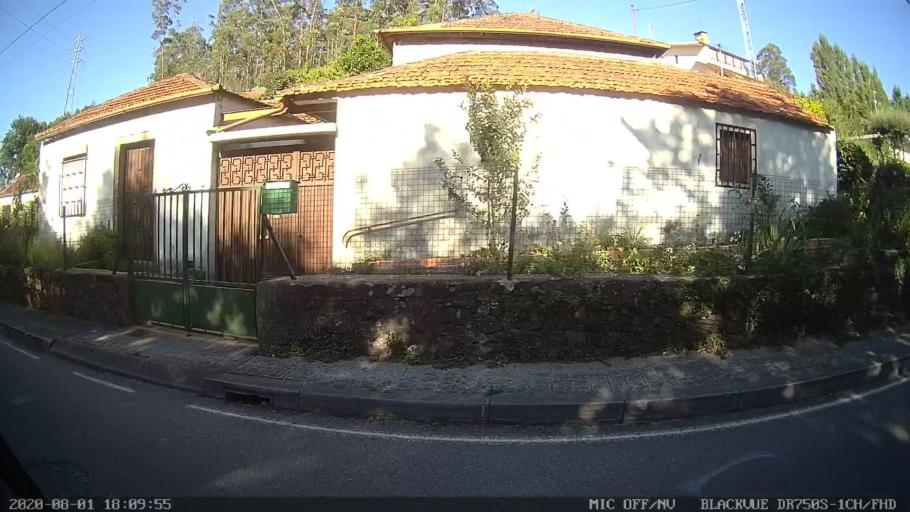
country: PT
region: Porto
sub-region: Santo Tirso
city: Sao Miguel do Couto
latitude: 41.3100
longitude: -8.4715
